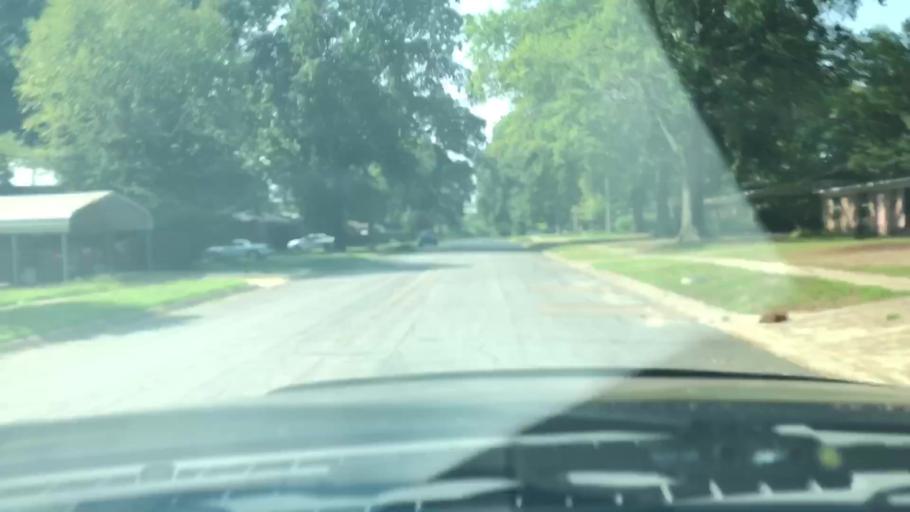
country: US
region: Arkansas
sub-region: Miller County
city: Texarkana
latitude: 33.4584
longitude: -94.0570
